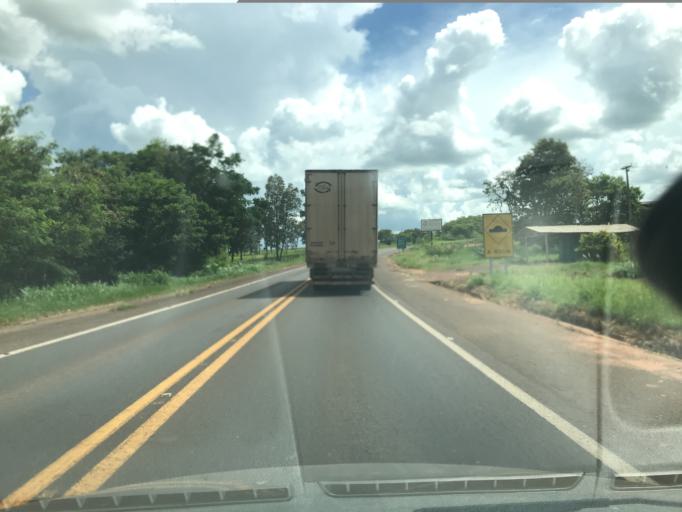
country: BR
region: Parana
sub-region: Cruzeiro Do Oeste
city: Cruzeiro do Oeste
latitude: -23.7971
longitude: -53.0500
